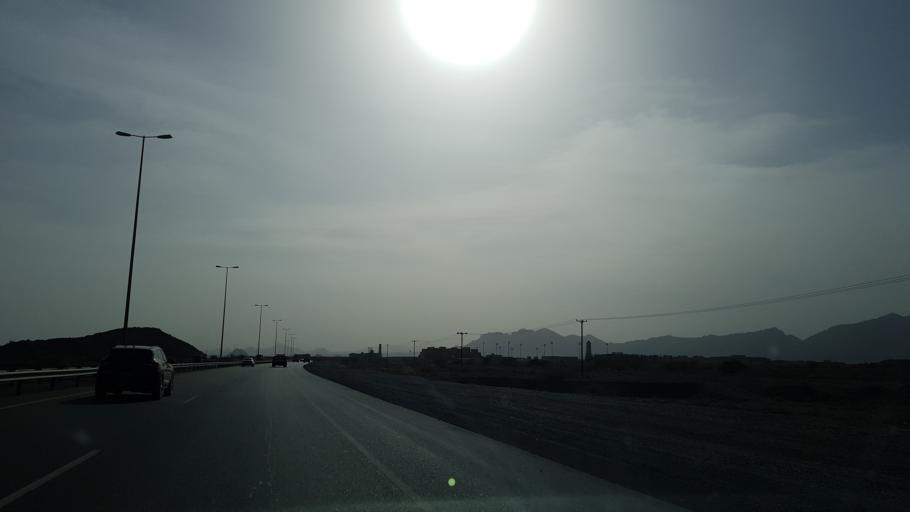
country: OM
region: Muhafazat ad Dakhiliyah
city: Nizwa
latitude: 22.8892
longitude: 57.6390
